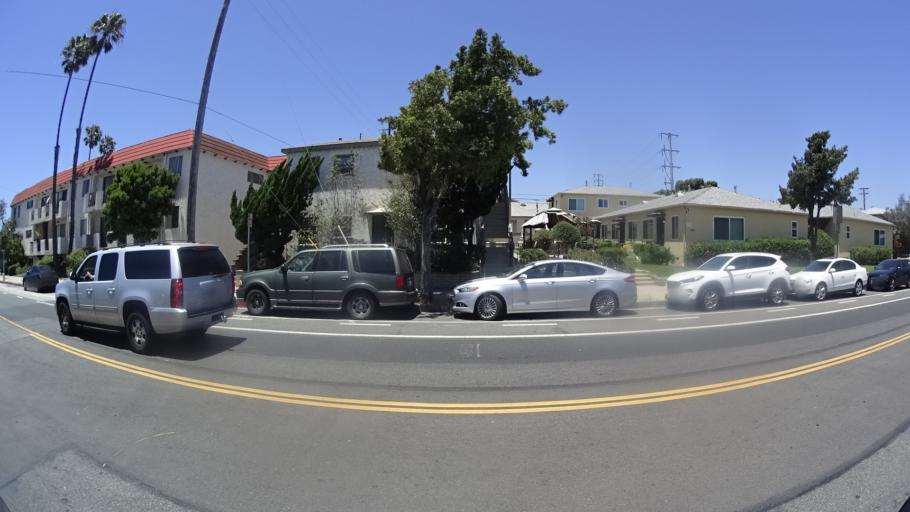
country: US
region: California
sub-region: Los Angeles County
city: Santa Monica
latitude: 34.0135
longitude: -118.4651
